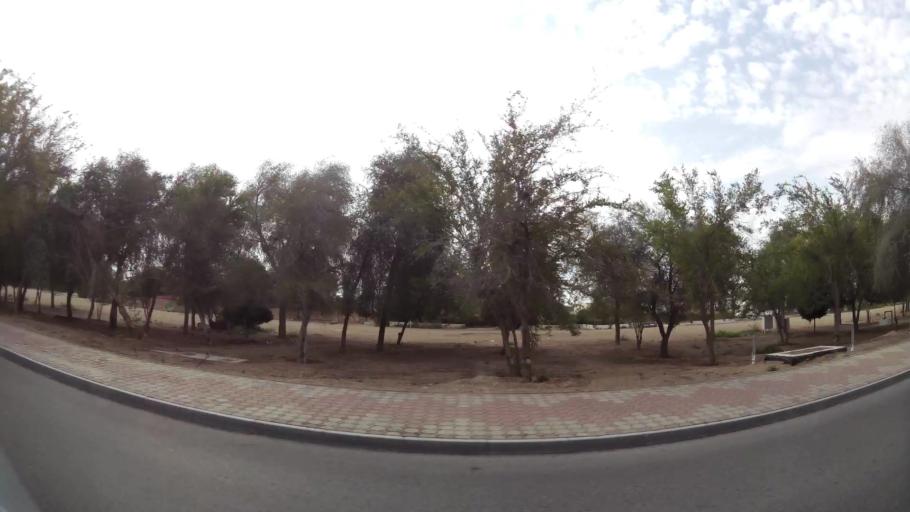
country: AE
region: Abu Dhabi
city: Al Ain
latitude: 24.1994
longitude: 55.6667
